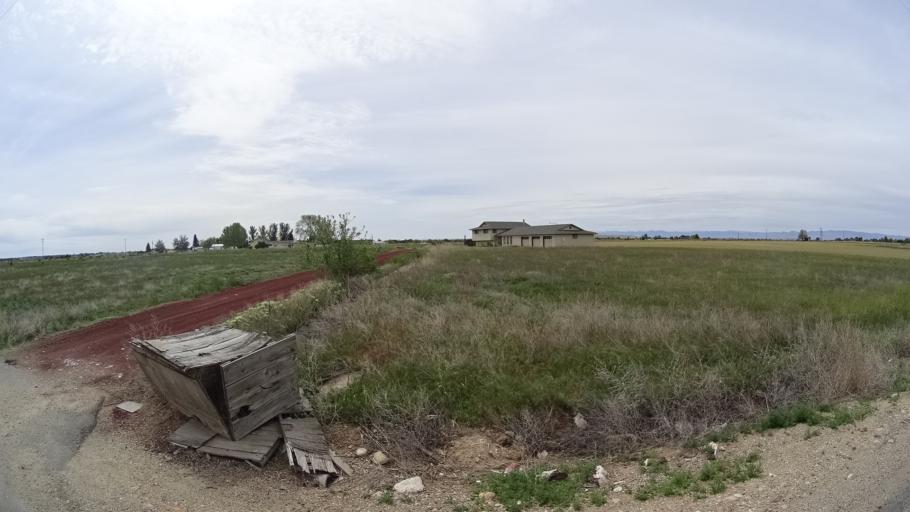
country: US
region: Idaho
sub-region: Ada County
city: Kuna
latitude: 43.5322
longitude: -116.4168
